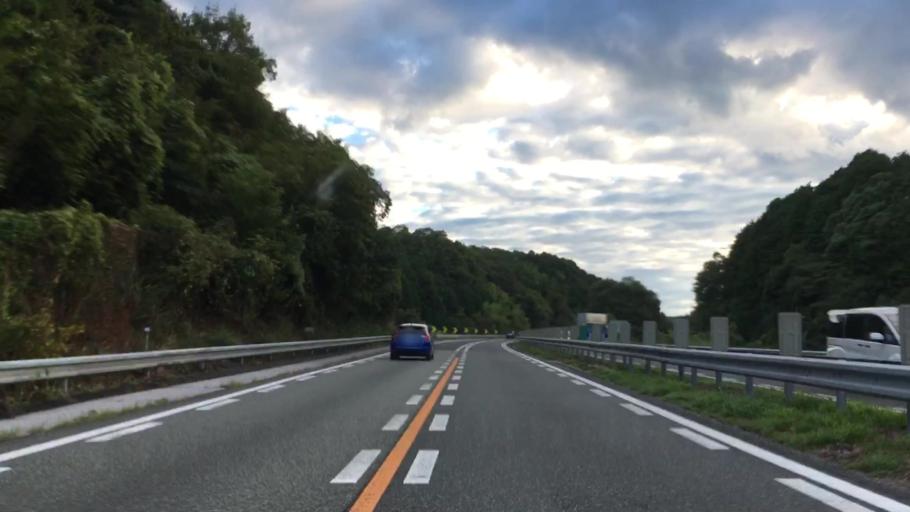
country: JP
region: Yamaguchi
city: Onoda
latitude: 34.1174
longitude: 131.1776
